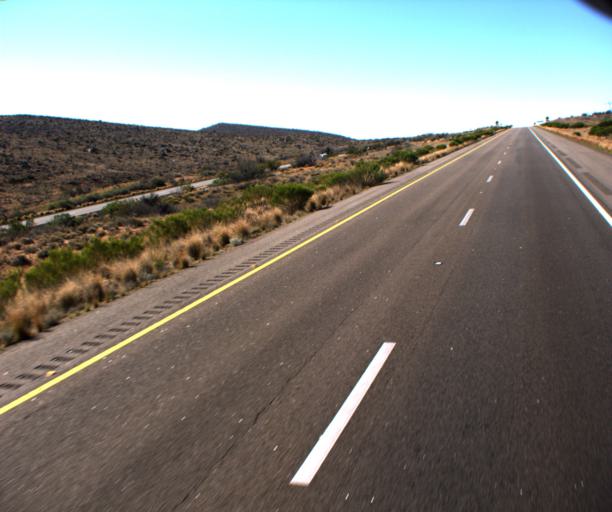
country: US
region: Arizona
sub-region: Mohave County
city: Kingman
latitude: 34.9616
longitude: -113.6705
